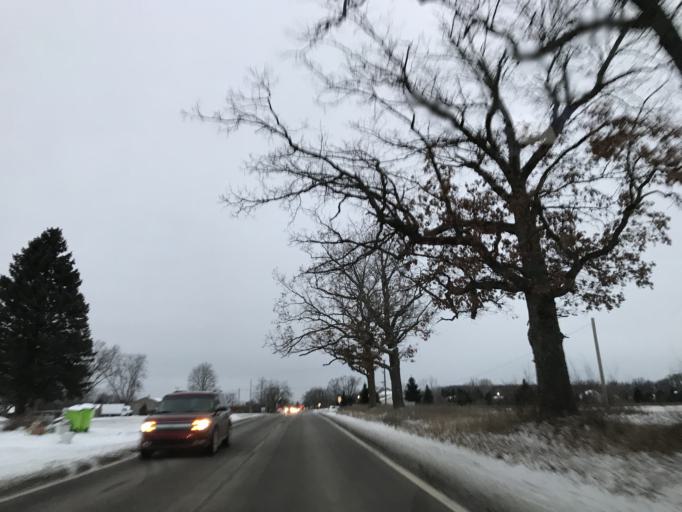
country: US
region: Michigan
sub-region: Oakland County
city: South Lyon
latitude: 42.4375
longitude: -83.6497
